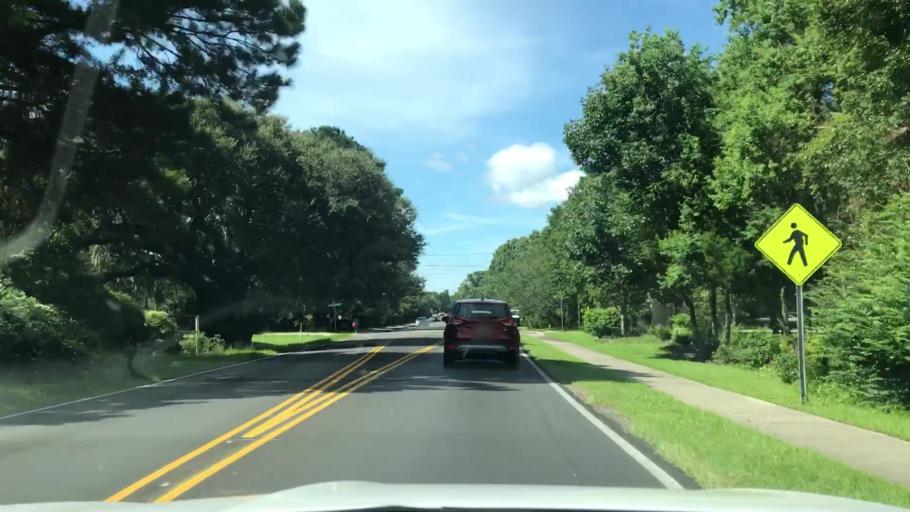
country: US
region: South Carolina
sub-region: Charleston County
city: North Charleston
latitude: 32.8180
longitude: -80.0389
